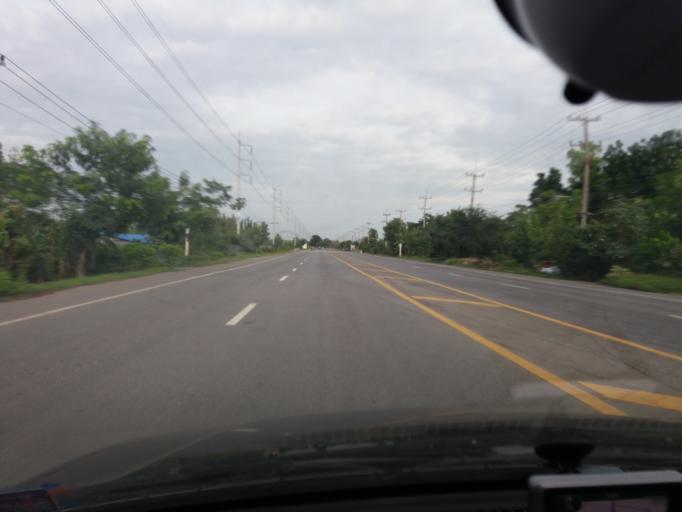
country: TH
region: Kanchanaburi
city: Huai Krachao
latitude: 14.3344
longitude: 99.7741
